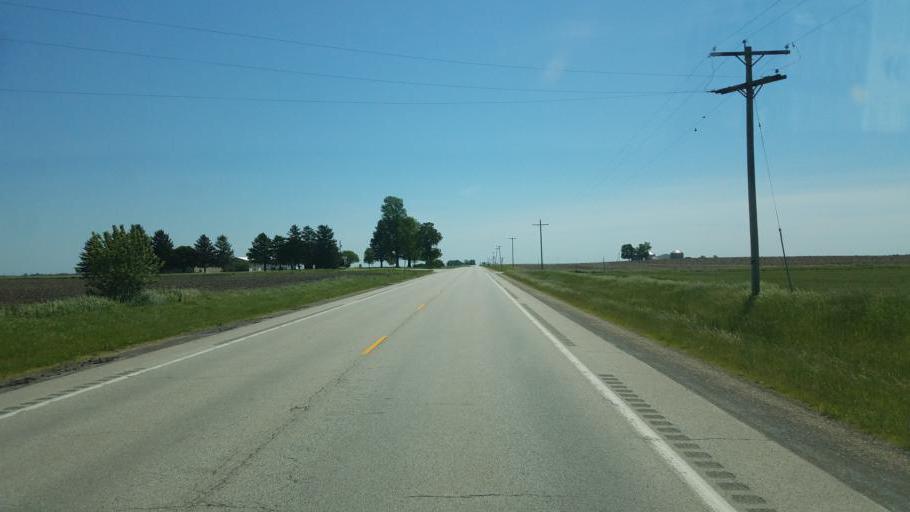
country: US
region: Illinois
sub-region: McLean County
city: Heyworth
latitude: 40.3123
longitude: -88.9022
